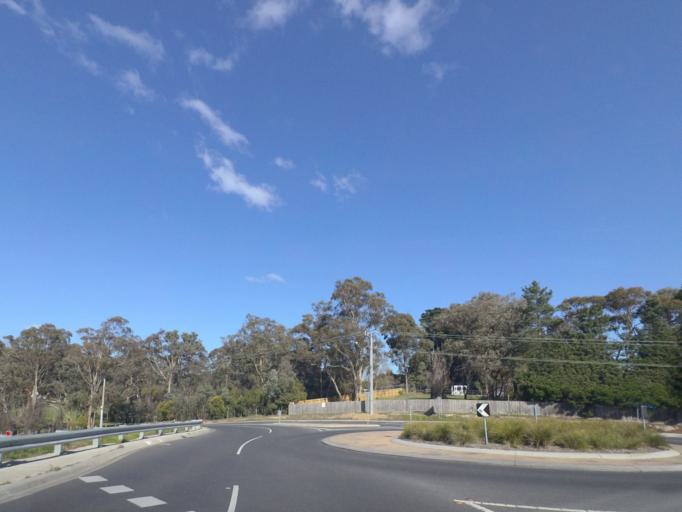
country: AU
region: Victoria
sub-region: Manningham
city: Park Orchards
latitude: -37.7714
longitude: 145.1996
